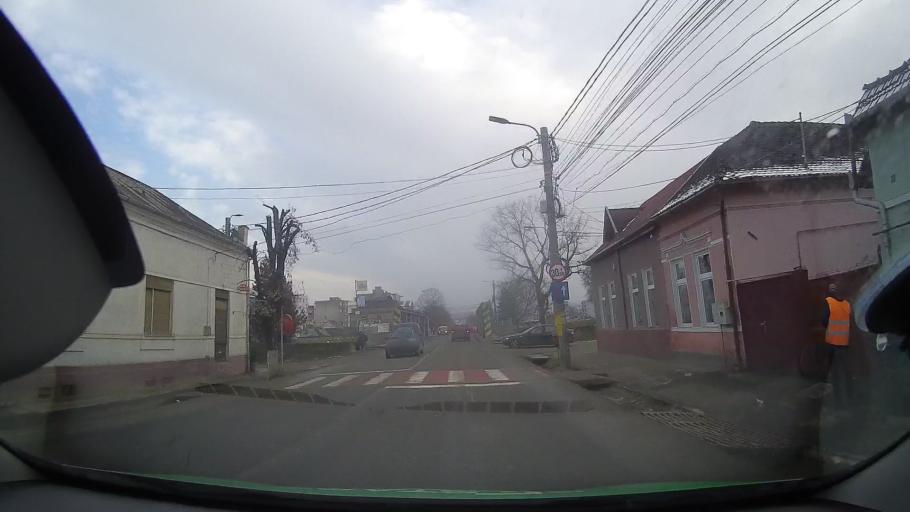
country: RO
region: Mures
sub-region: Municipiul Tarnaveni
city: Tarnaveni
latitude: 46.3327
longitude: 24.2942
